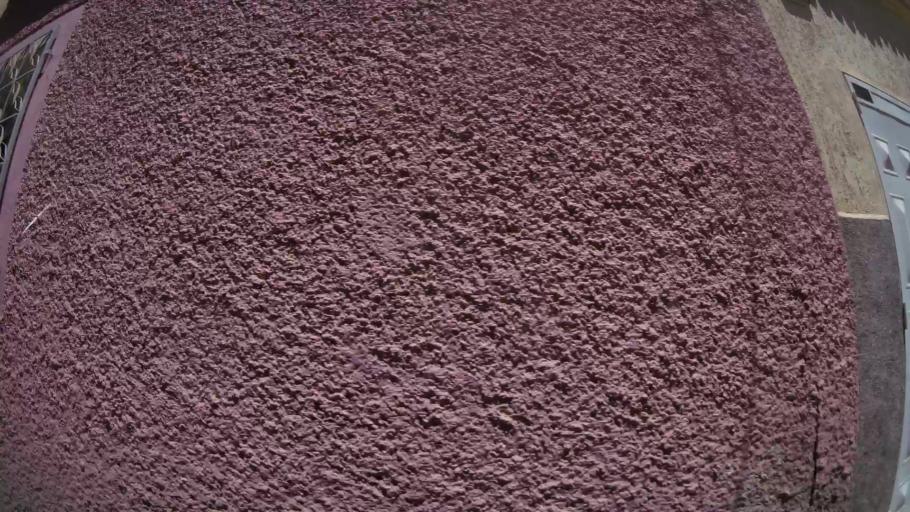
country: MA
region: Oriental
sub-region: Oujda-Angad
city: Oujda
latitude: 34.6752
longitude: -1.8851
